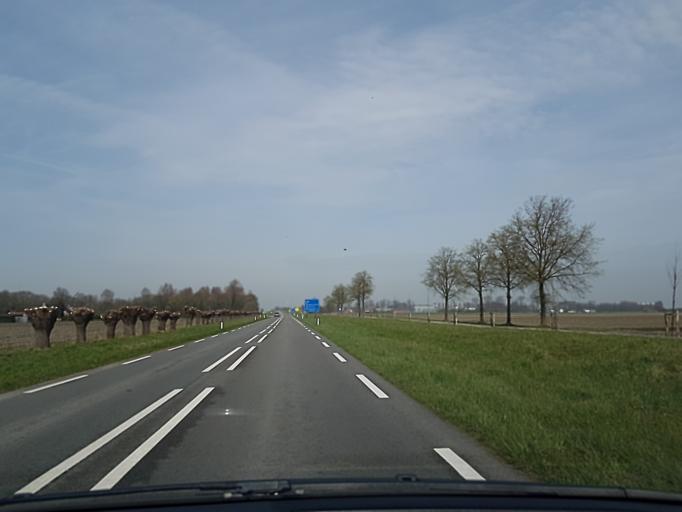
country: NL
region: Zeeland
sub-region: Gemeente Hulst
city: Hulst
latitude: 51.3672
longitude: 4.0238
